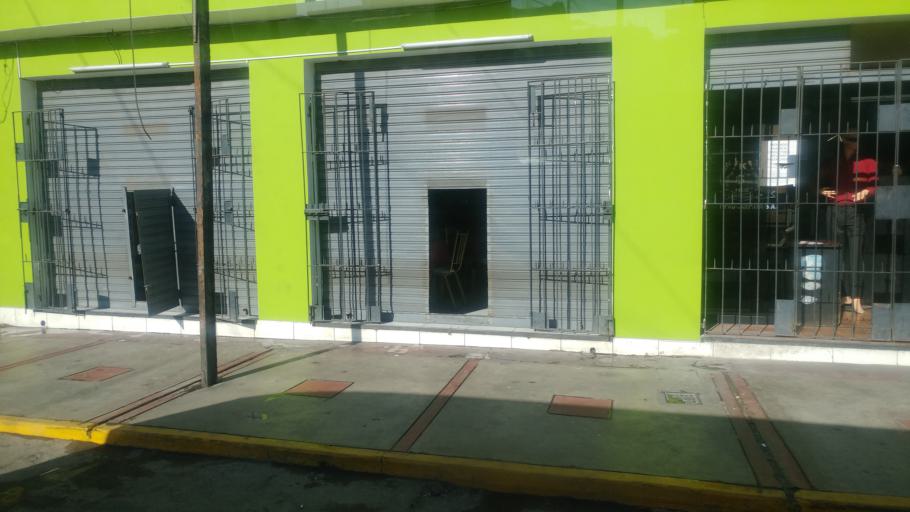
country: PE
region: Arequipa
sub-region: Provincia de Arequipa
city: Arequipa
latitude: -16.4252
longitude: -71.5054
